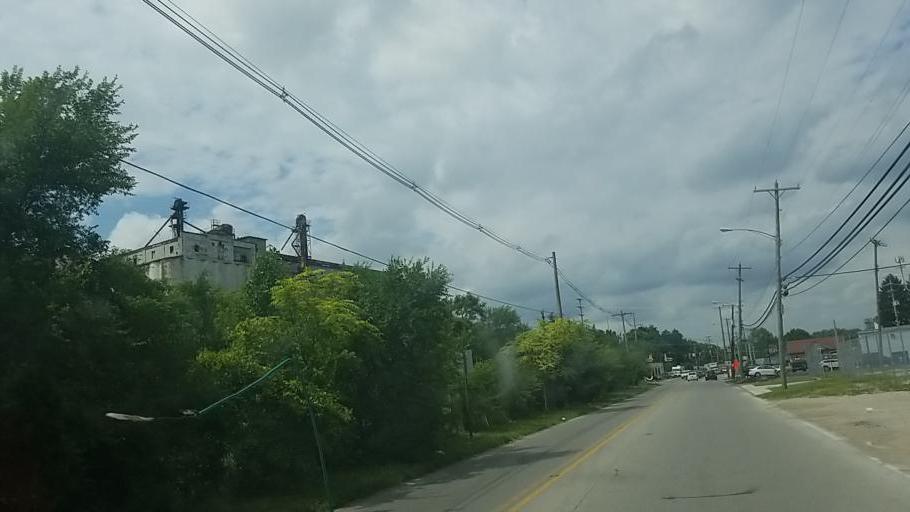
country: US
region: Ohio
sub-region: Franklin County
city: Bexley
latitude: 39.9559
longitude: -82.9469
